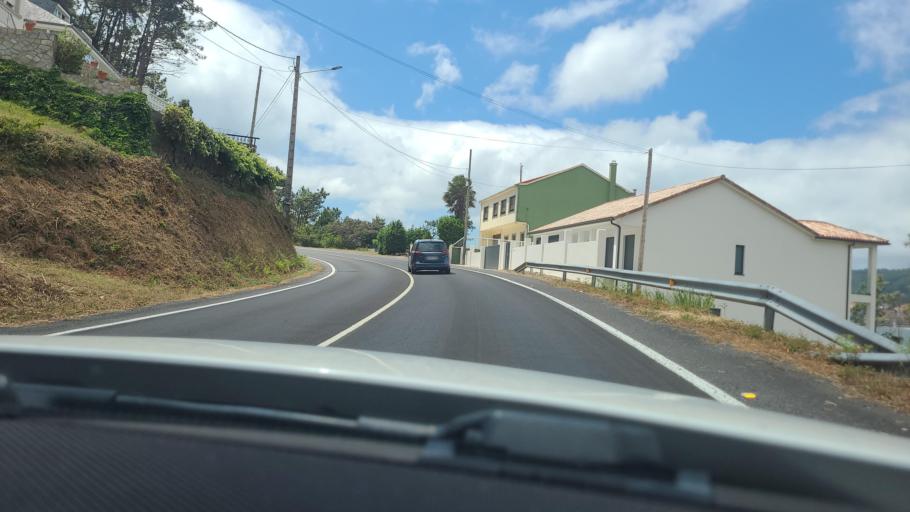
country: ES
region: Galicia
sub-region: Provincia da Coruna
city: Cee
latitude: 42.9422
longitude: -9.1729
